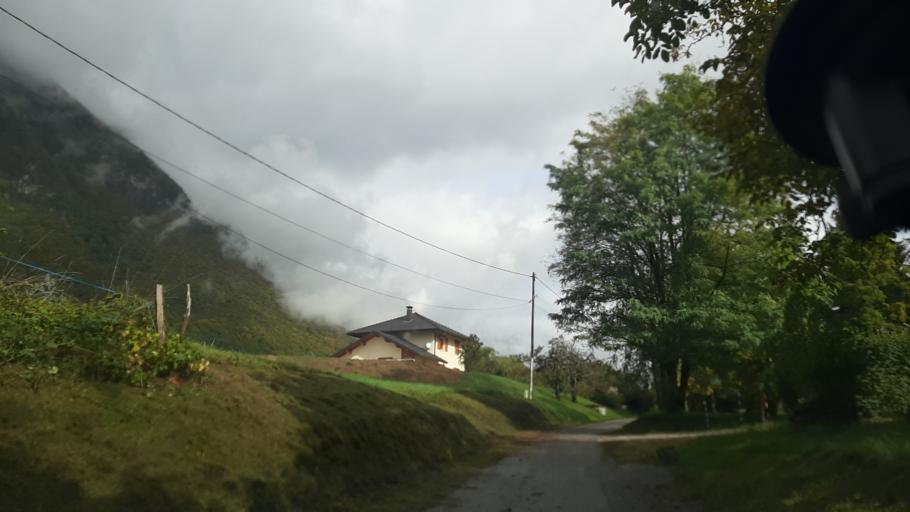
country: FR
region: Rhone-Alpes
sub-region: Departement de la Savoie
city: Gresy-sur-Isere
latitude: 45.6055
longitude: 6.2676
